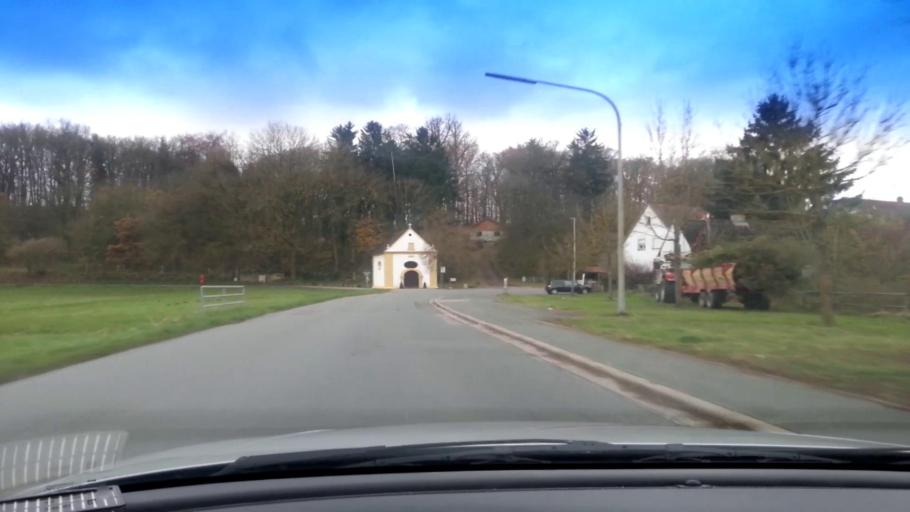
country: DE
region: Bavaria
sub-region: Upper Franconia
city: Stegaurach
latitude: 49.8612
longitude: 10.8413
